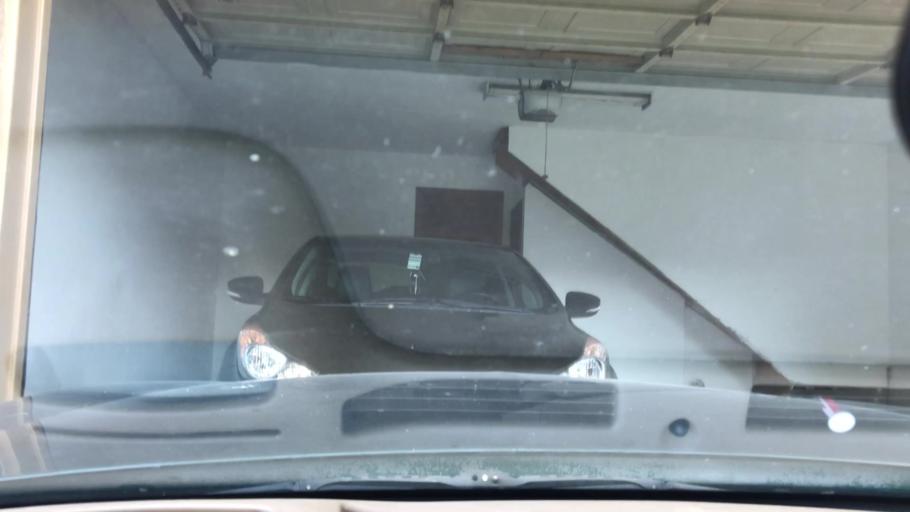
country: US
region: Tennessee
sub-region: Shelby County
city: Lakeland
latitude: 35.1960
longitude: -89.7992
